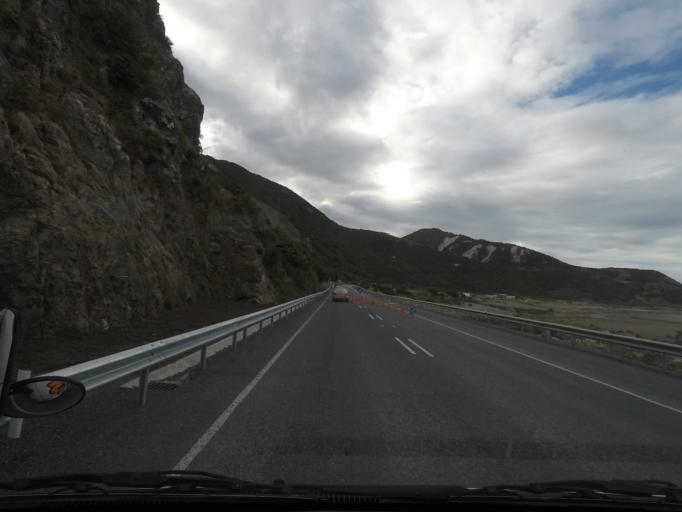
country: NZ
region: Canterbury
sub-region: Kaikoura District
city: Kaikoura
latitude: -42.2206
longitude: 173.8569
